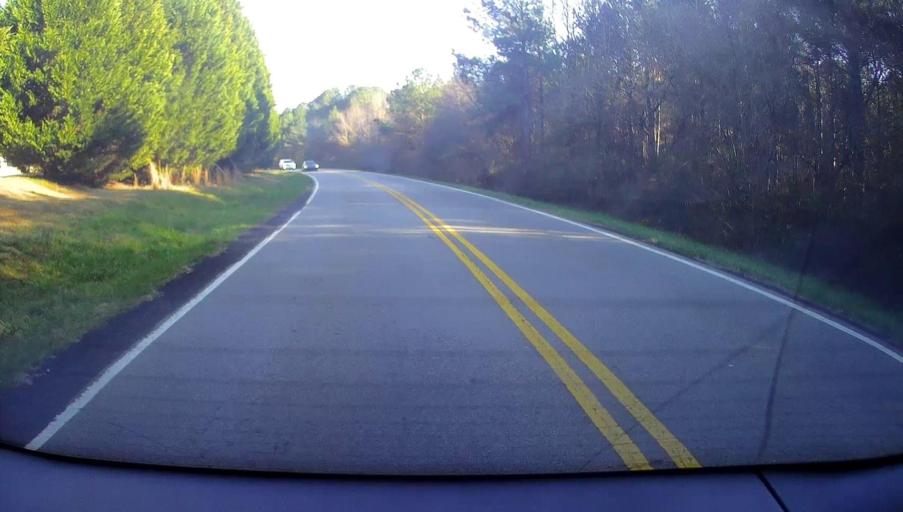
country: US
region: Georgia
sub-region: Henry County
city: Locust Grove
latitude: 33.3609
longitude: -84.1758
